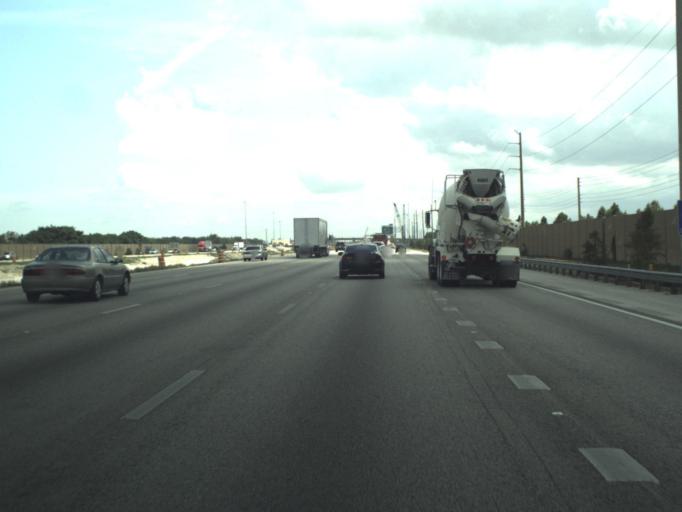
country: US
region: Florida
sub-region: Miami-Dade County
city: Palm Springs North
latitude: 25.9657
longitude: -80.3525
